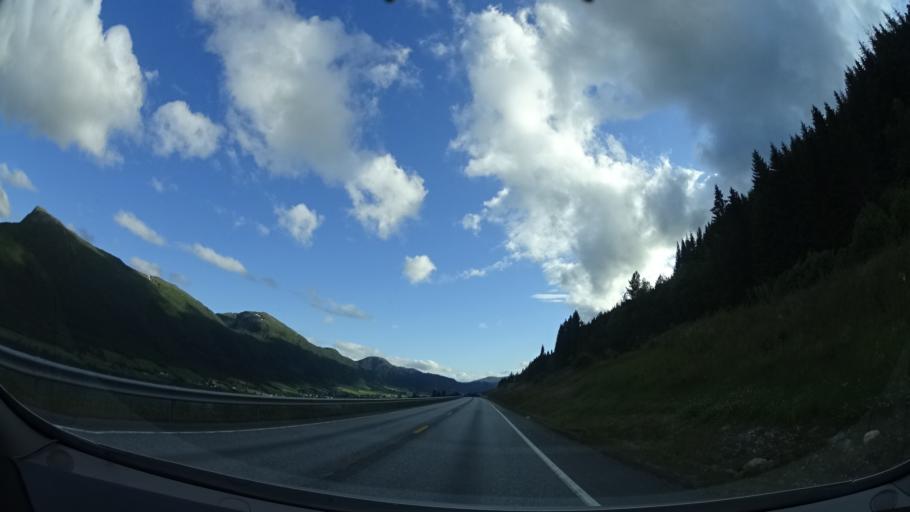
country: NO
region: More og Romsdal
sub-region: Gjemnes
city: Batnfjordsora
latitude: 62.9154
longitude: 7.6917
